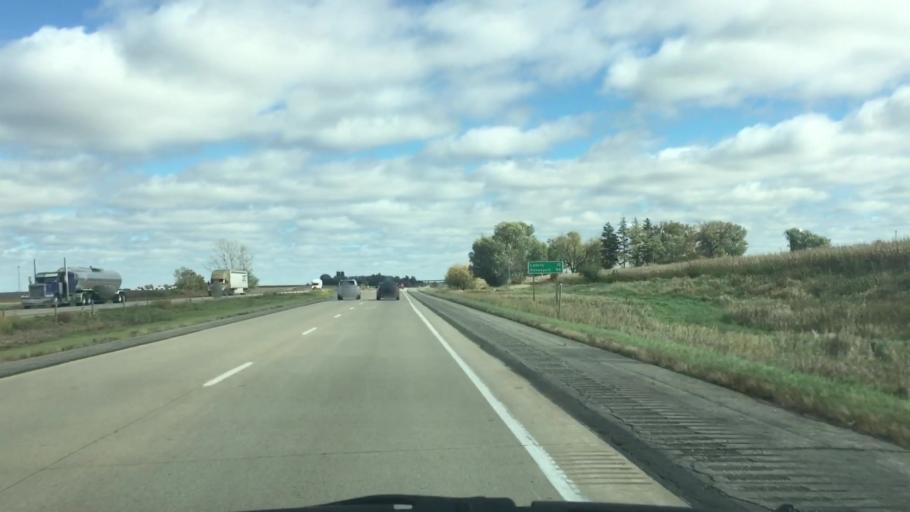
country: US
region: Iowa
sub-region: Poweshiek County
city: Brooklyn
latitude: 41.6962
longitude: -92.2640
